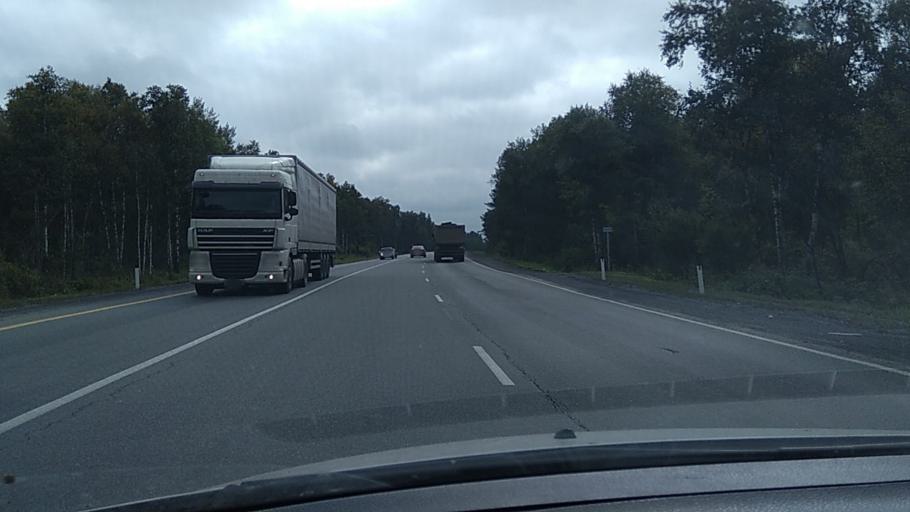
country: RU
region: Chelyabinsk
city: Zlatoust
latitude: 55.0433
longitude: 59.7247
